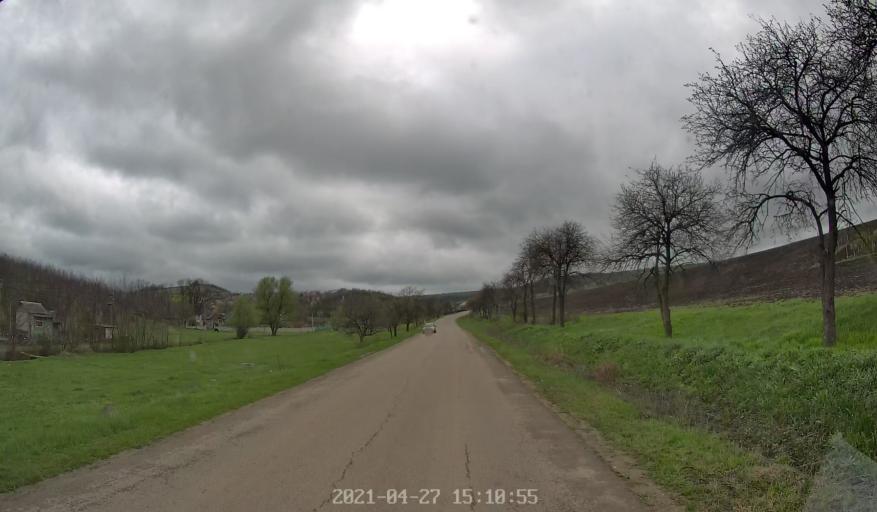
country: MD
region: Chisinau
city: Vadul lui Voda
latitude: 47.0358
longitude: 29.0312
